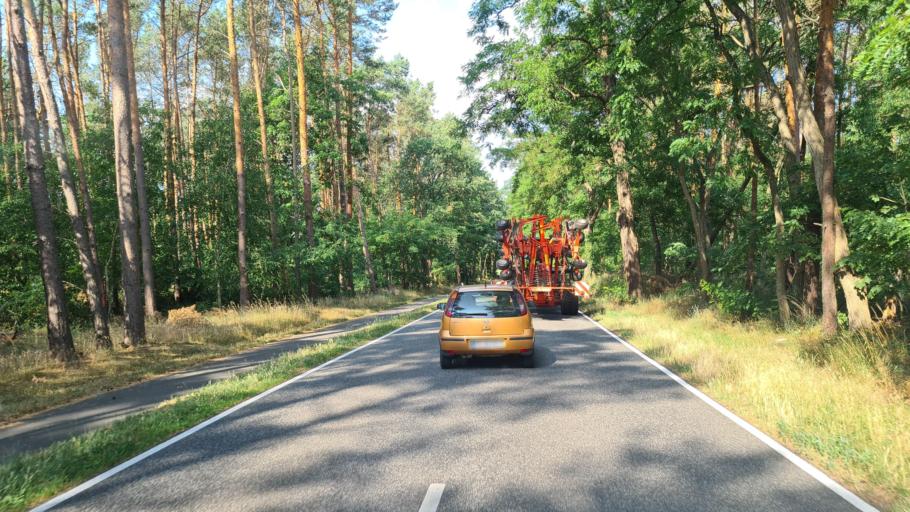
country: DE
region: Brandenburg
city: Golzow
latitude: 52.3287
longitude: 12.5864
